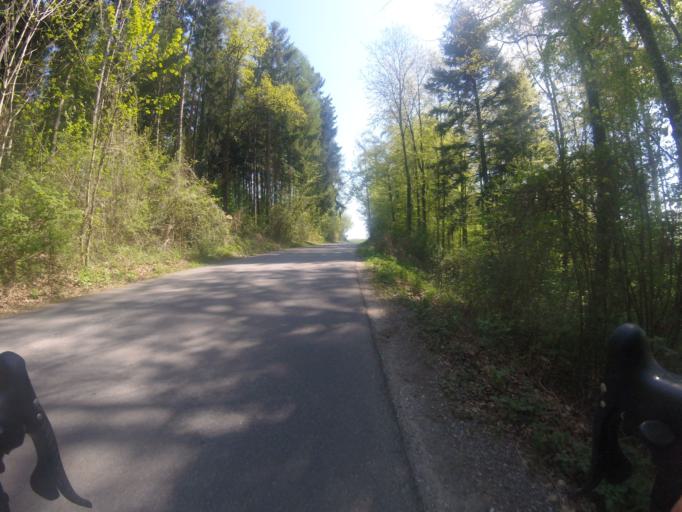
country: CH
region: Bern
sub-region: Bern-Mittelland District
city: Laupen
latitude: 46.9010
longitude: 7.2561
